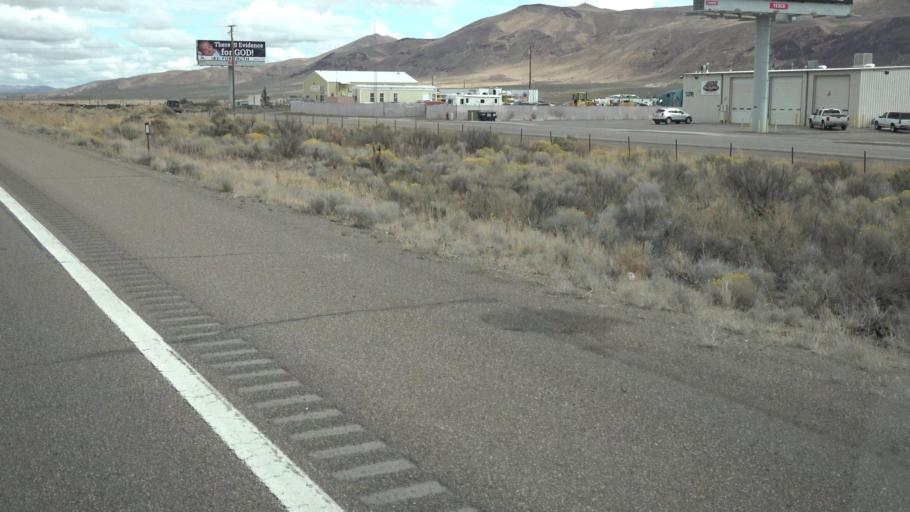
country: US
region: Nevada
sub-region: Elko County
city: Elko
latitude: 40.8753
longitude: -115.7222
